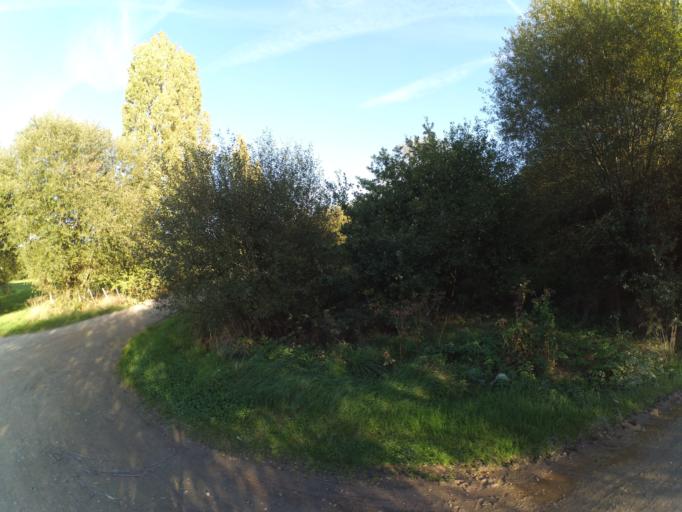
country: FR
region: Brittany
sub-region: Departement du Morbihan
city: Saint-Vincent-sur-Oust
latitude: 47.7194
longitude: -2.1476
